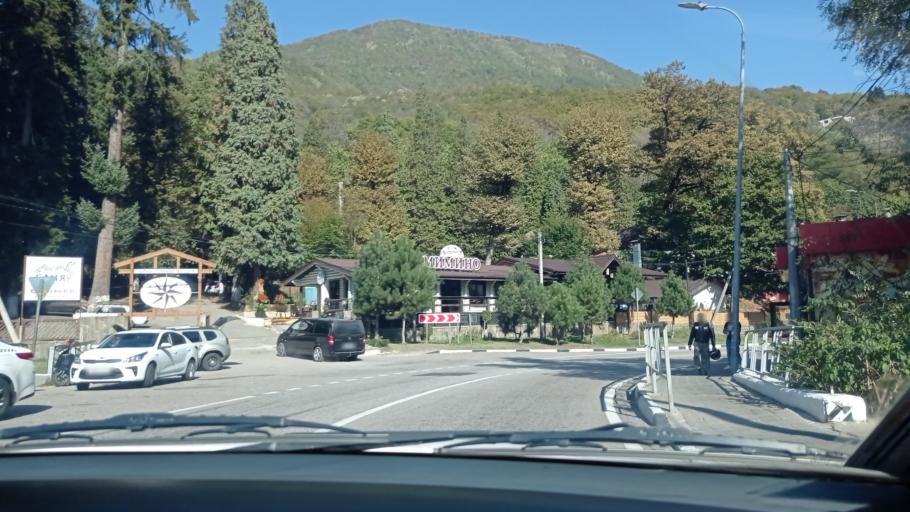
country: RU
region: Krasnodarskiy
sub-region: Sochi City
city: Krasnaya Polyana
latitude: 43.6824
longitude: 40.2128
